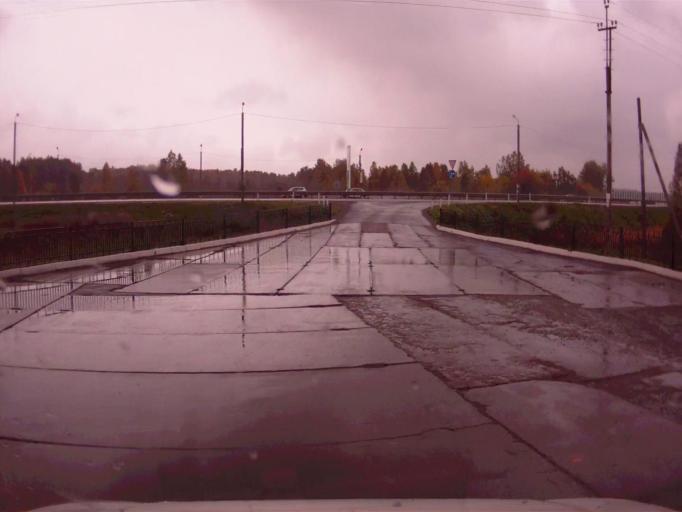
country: RU
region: Chelyabinsk
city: Dolgoderevenskoye
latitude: 55.3006
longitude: 61.3374
